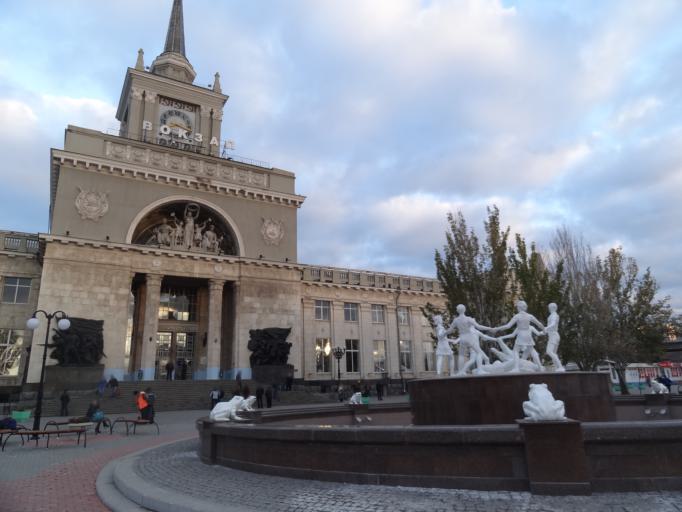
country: RU
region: Volgograd
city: Volgograd
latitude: 48.7120
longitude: 44.5138
